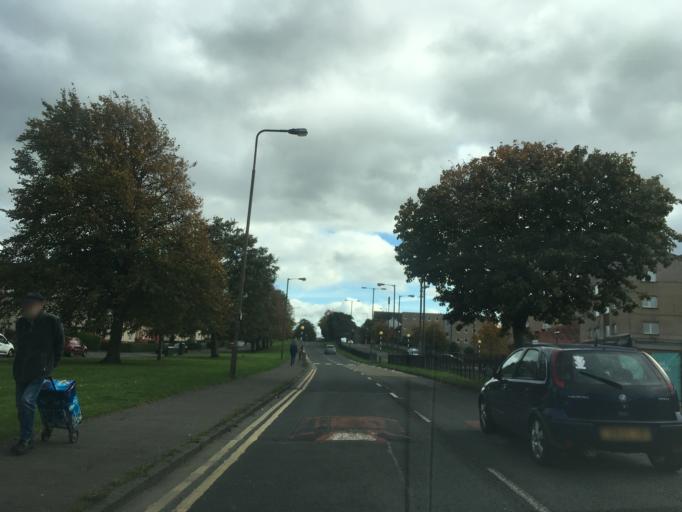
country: GB
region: Scotland
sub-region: Edinburgh
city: Edinburgh
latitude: 55.9721
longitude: -3.2525
